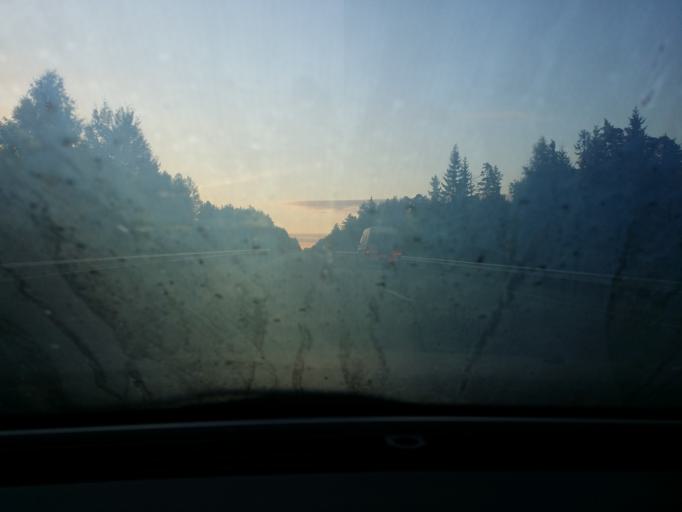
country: SE
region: Uppsala
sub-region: Enkopings Kommun
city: Grillby
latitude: 59.6311
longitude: 17.3245
